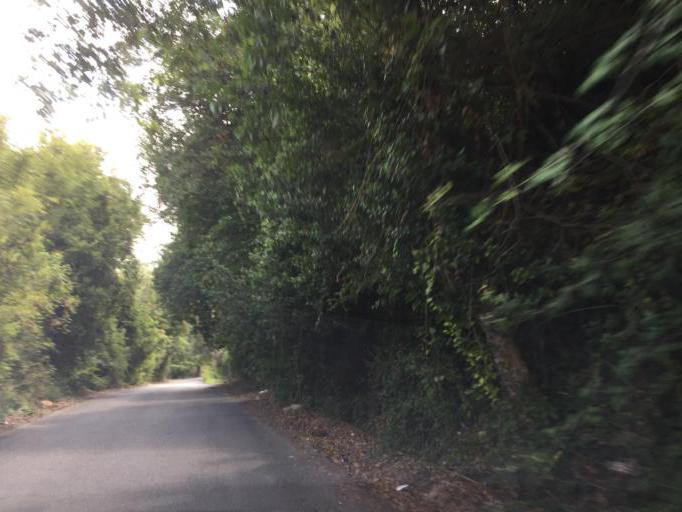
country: LB
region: Mont-Liban
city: Beit ed Dine
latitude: 33.6953
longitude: 35.5773
